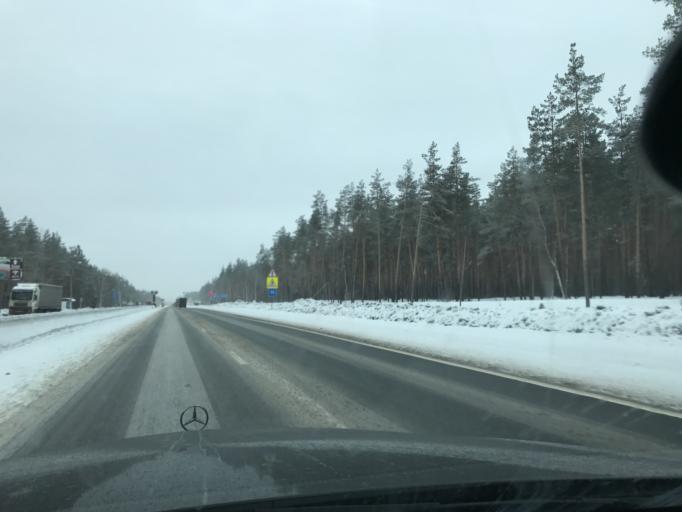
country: RU
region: Nizjnij Novgorod
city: Pyra
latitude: 56.2950
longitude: 43.3937
